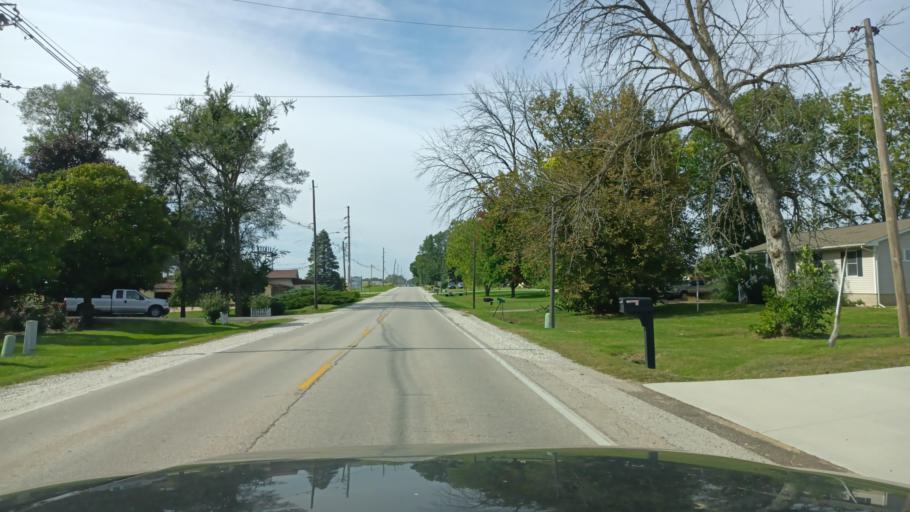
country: US
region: Illinois
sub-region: Knox County
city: Knoxville
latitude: 40.9123
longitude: -90.2973
